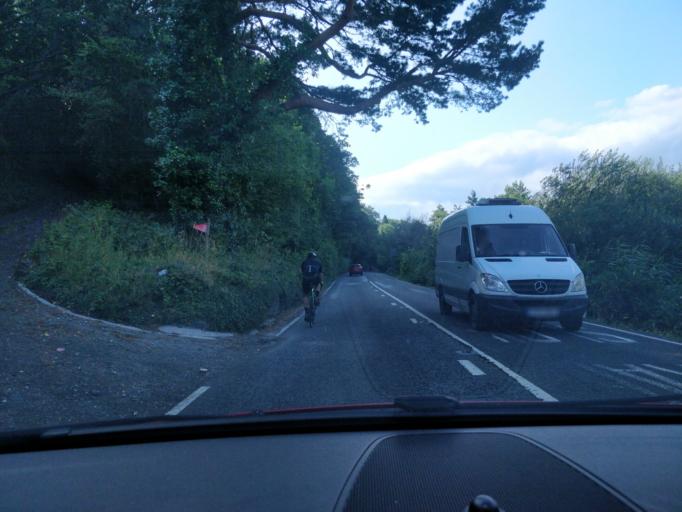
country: GB
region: Wales
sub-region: Conwy
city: Llanrwst
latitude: 53.1942
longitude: -3.8269
